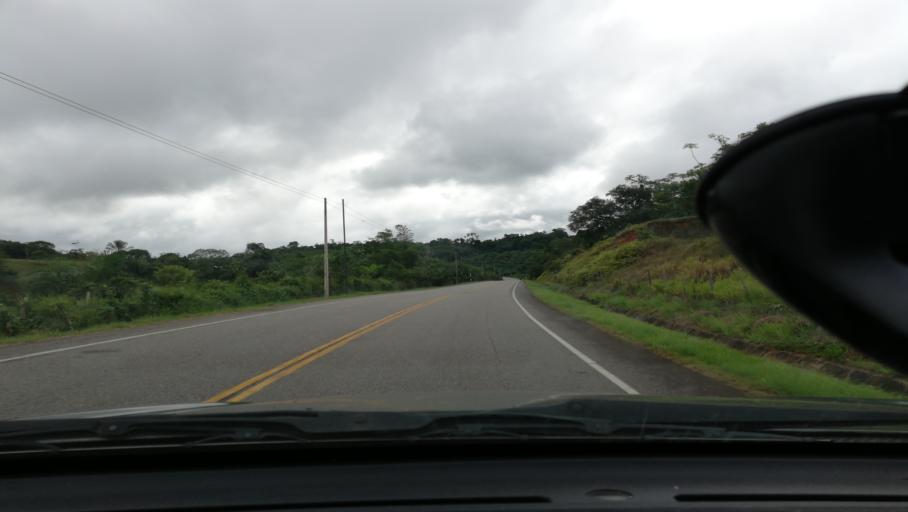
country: PE
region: Loreto
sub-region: Provincia de Loreto
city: Nauta
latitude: -4.4854
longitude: -73.5985
